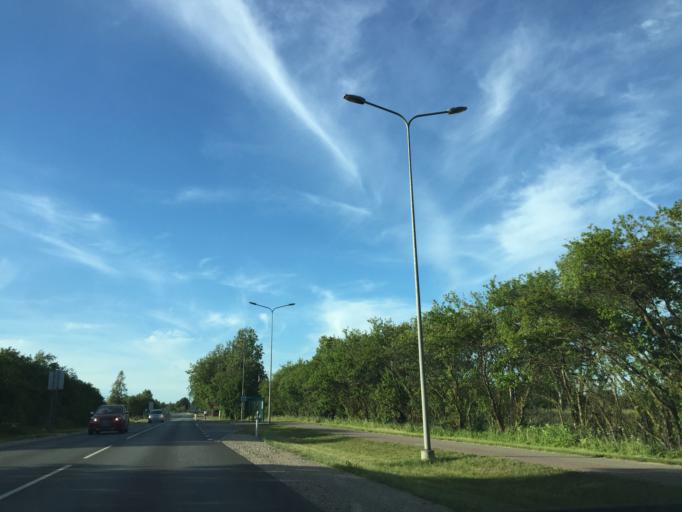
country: LV
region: Ventspils
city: Ventspils
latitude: 57.3642
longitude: 21.5635
